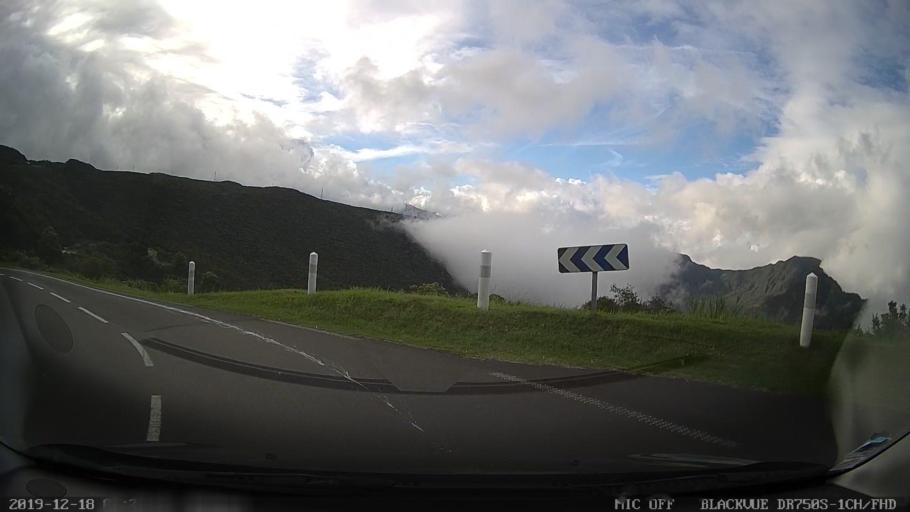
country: RE
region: Reunion
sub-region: Reunion
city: Cilaos
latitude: -21.1617
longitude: 55.5969
